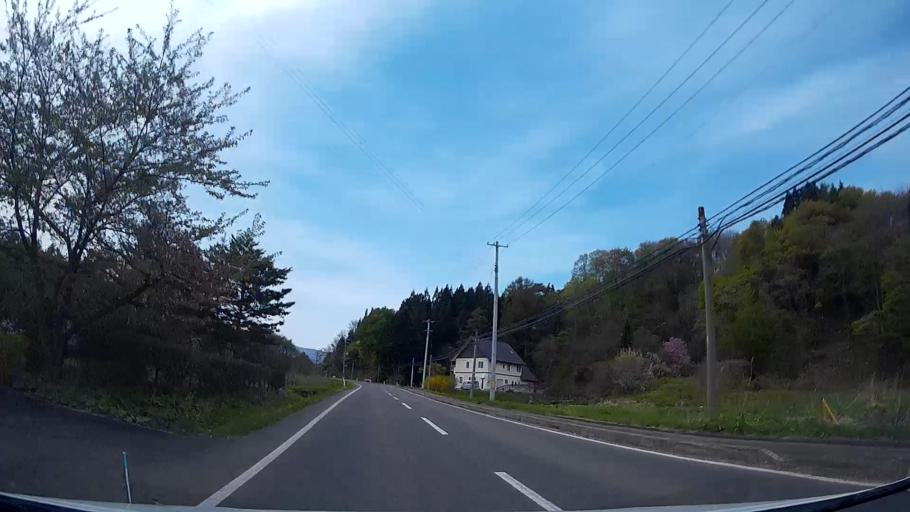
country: JP
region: Iwate
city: Shizukuishi
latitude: 39.9292
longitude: 140.9856
